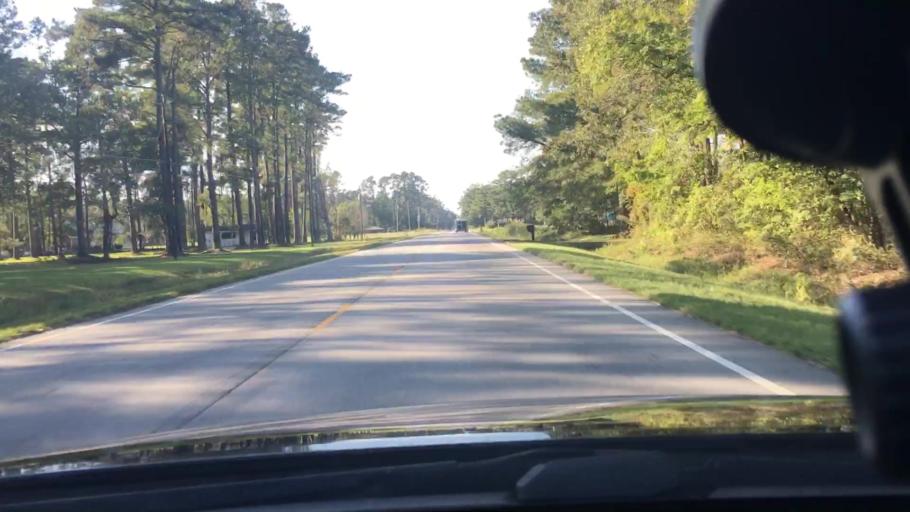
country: US
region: North Carolina
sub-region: Craven County
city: Vanceboro
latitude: 35.2552
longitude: -77.0949
